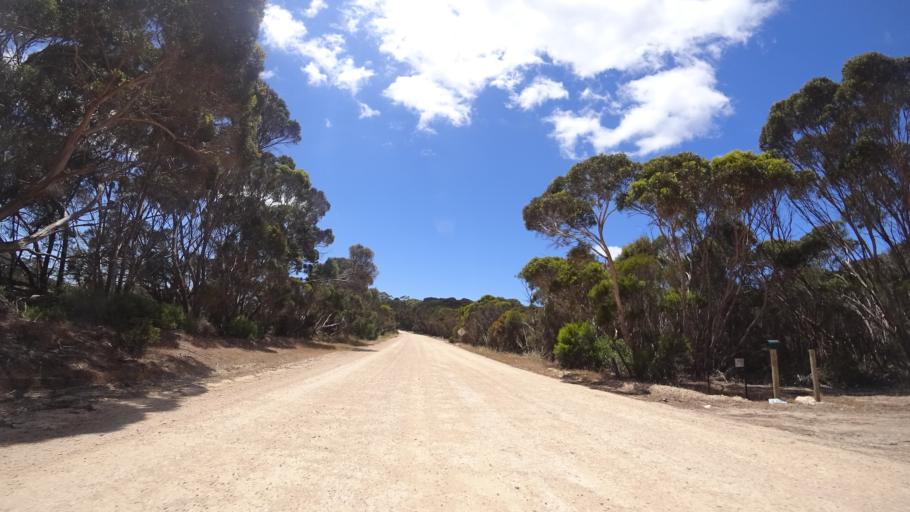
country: AU
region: South Australia
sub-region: Kangaroo Island
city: Kingscote
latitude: -35.8220
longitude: 138.0491
